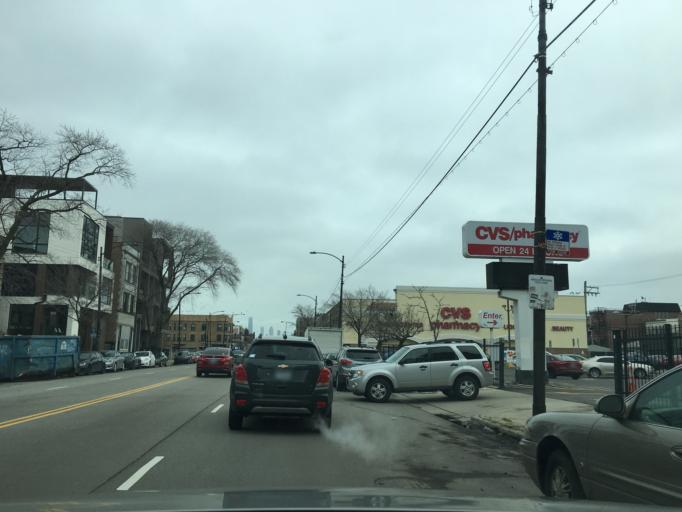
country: US
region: Illinois
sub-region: Cook County
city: Chicago
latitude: 41.8957
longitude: -87.6889
